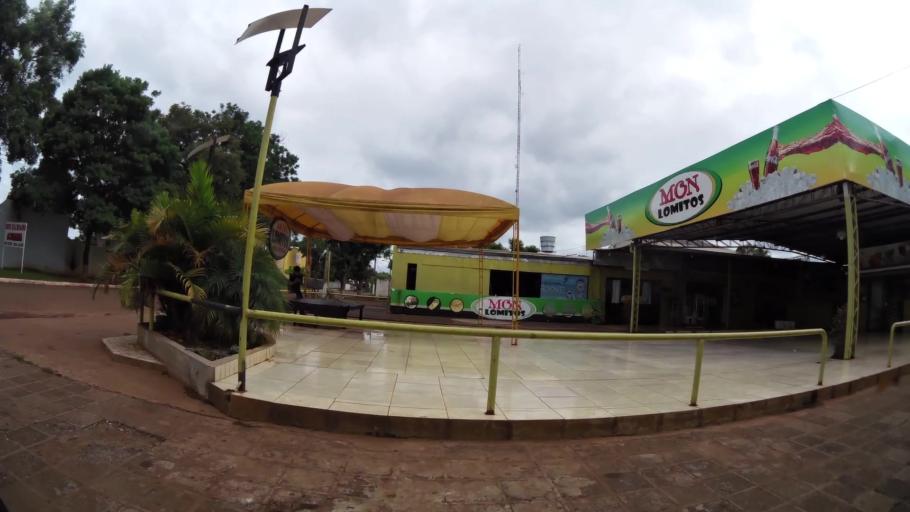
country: PY
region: Alto Parana
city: Ciudad del Este
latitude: -25.4062
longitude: -54.6401
